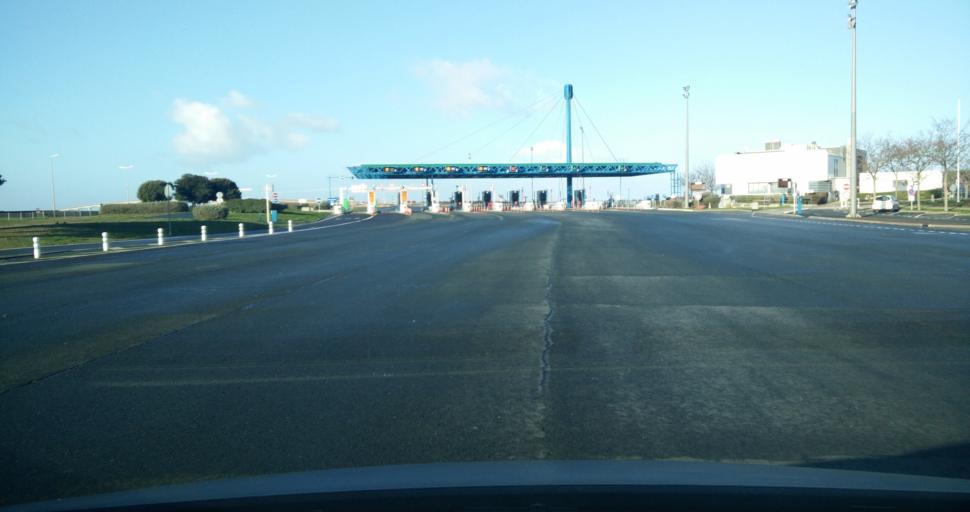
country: FR
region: Poitou-Charentes
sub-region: Departement de la Charente-Maritime
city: Rivedoux-Plage
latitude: 46.1757
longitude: -1.2172
